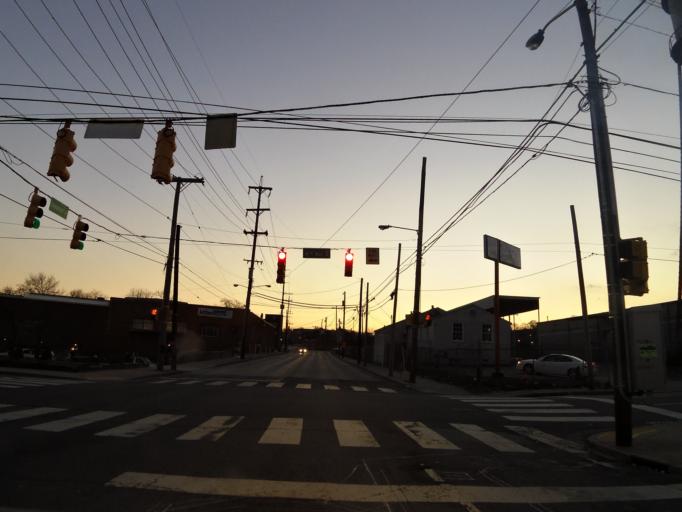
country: US
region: Tennessee
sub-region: Davidson County
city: Nashville
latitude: 36.1450
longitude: -86.7666
